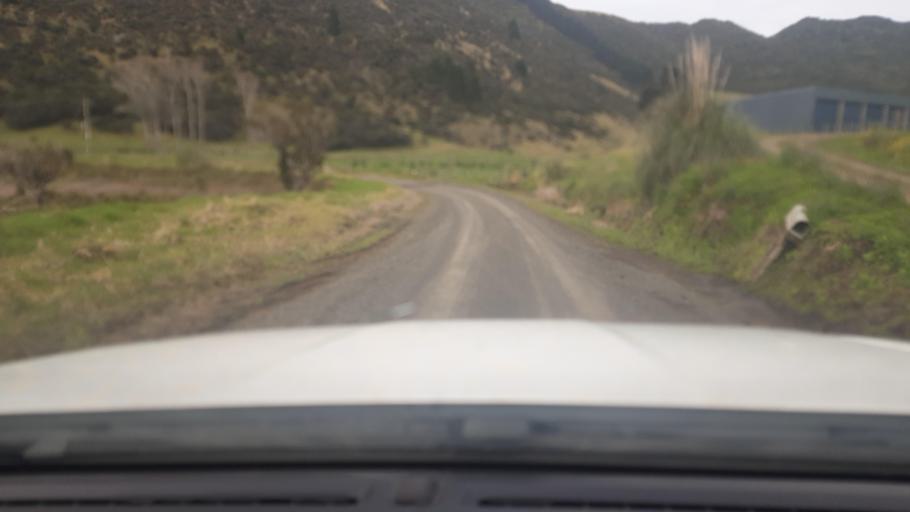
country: NZ
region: Northland
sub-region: Far North District
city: Ahipara
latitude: -35.3341
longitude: 173.2203
